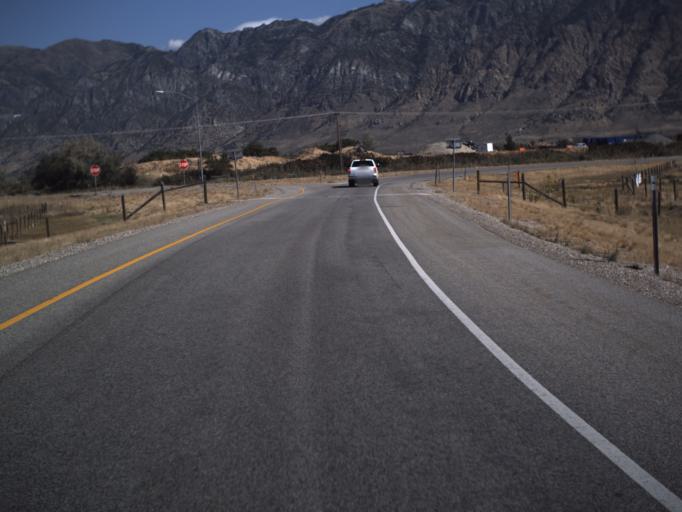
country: US
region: Utah
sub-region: Box Elder County
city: Brigham City
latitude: 41.5085
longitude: -112.0578
